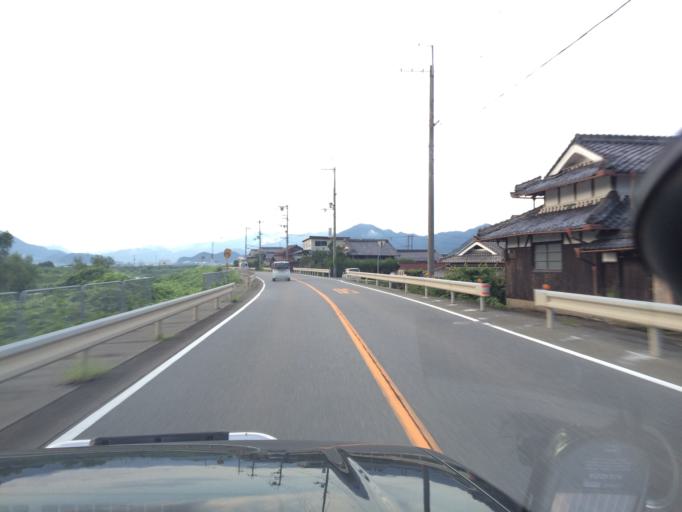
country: JP
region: Hyogo
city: Nishiwaki
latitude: 35.1398
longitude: 135.0278
